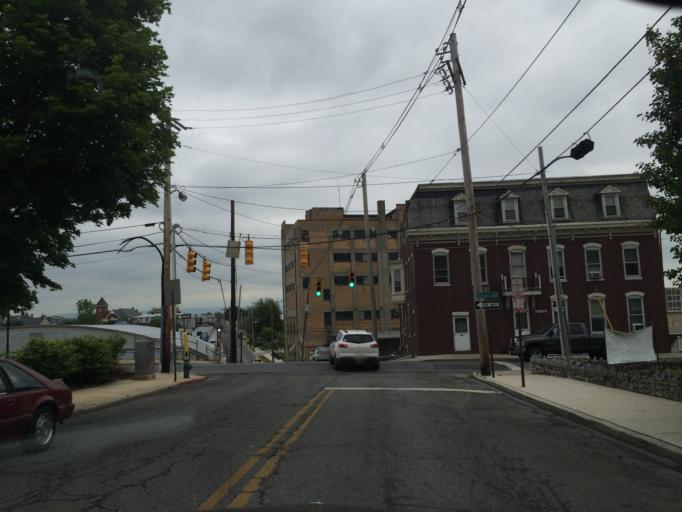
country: US
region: Maryland
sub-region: Washington County
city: Hagerstown
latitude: 39.6399
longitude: -77.7258
